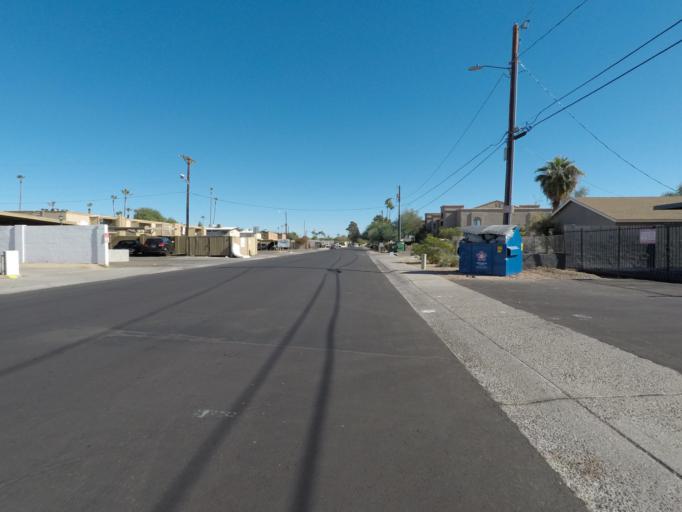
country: US
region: Arizona
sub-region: Maricopa County
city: Phoenix
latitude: 33.5158
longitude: -112.0932
